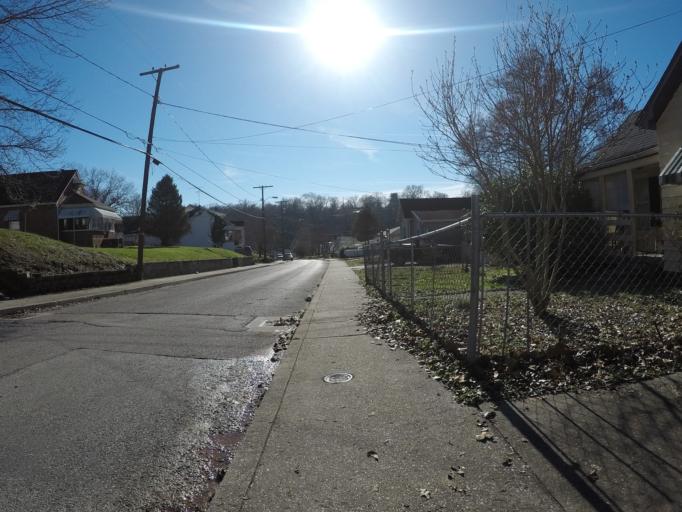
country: US
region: West Virginia
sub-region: Cabell County
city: Huntington
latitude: 38.4111
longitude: -82.3984
